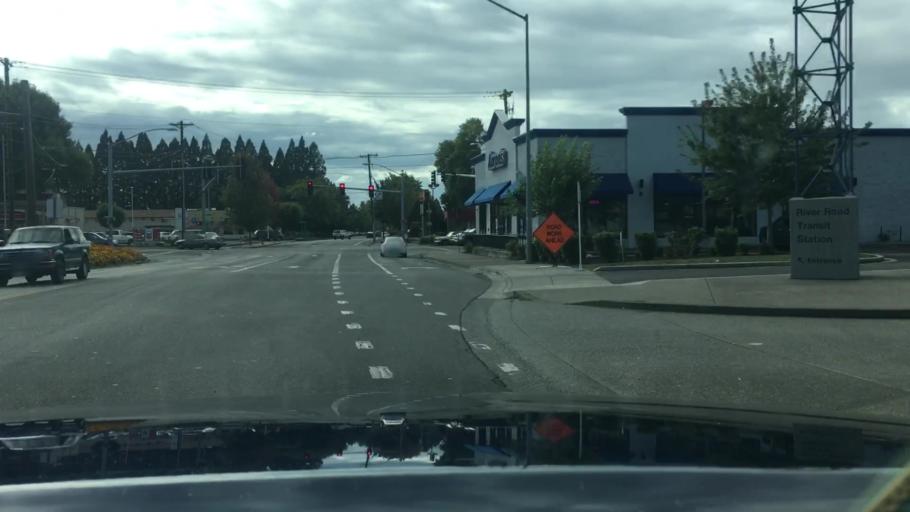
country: US
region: Oregon
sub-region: Lane County
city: Eugene
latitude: 44.0957
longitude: -123.1270
